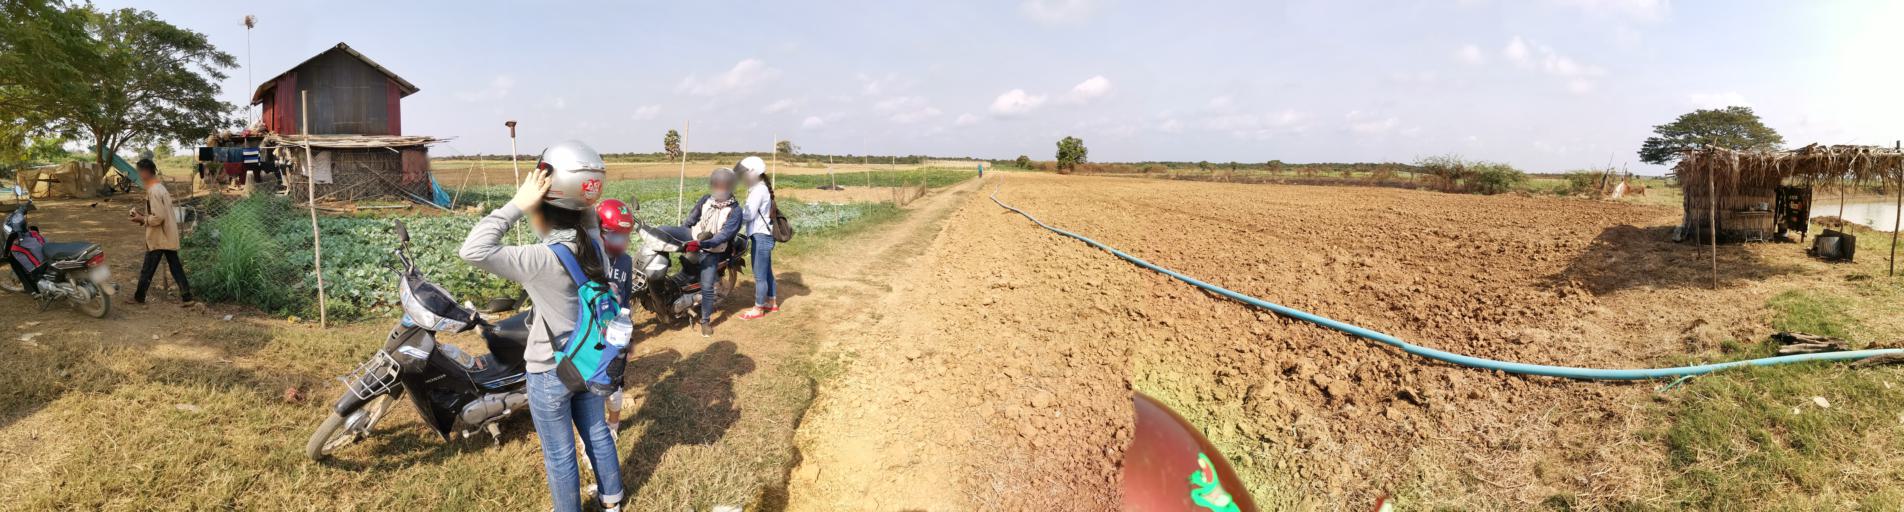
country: KH
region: Battambang
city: Battambang
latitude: 13.2458
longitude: 103.3264
